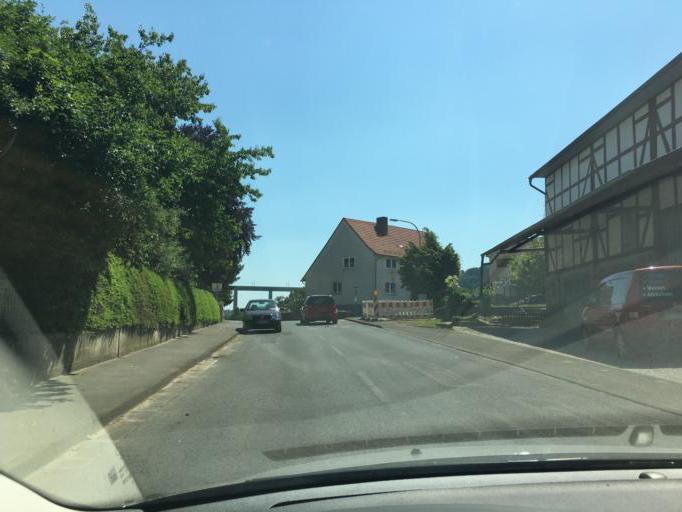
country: DE
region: Hesse
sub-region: Regierungsbezirk Kassel
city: Malsfeld
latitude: 51.0708
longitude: 9.5711
